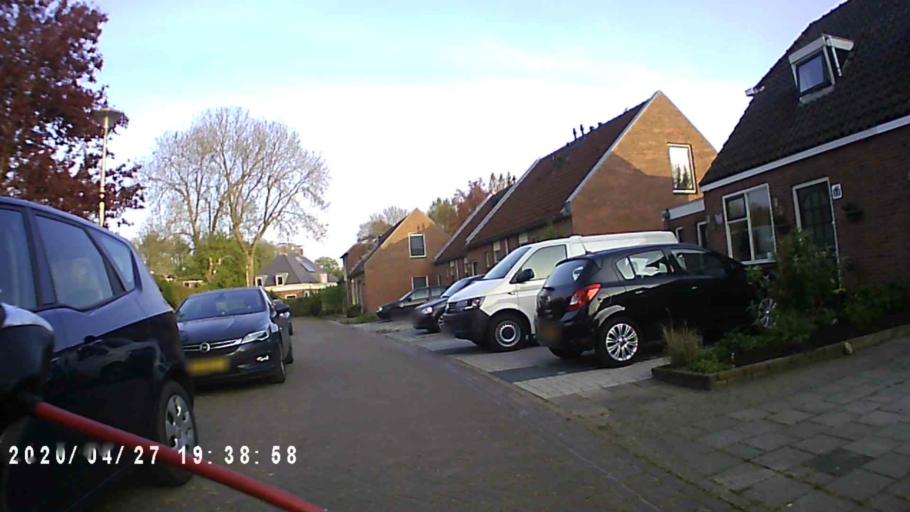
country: NL
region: Groningen
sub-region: Gemeente Winsum
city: Winsum
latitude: 53.3638
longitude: 6.4593
